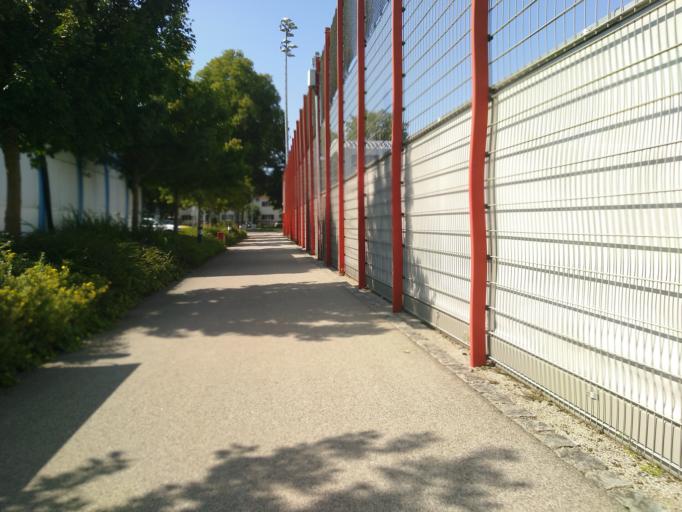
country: DE
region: Bavaria
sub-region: Upper Bavaria
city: Munich
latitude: 48.0999
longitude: 11.5729
